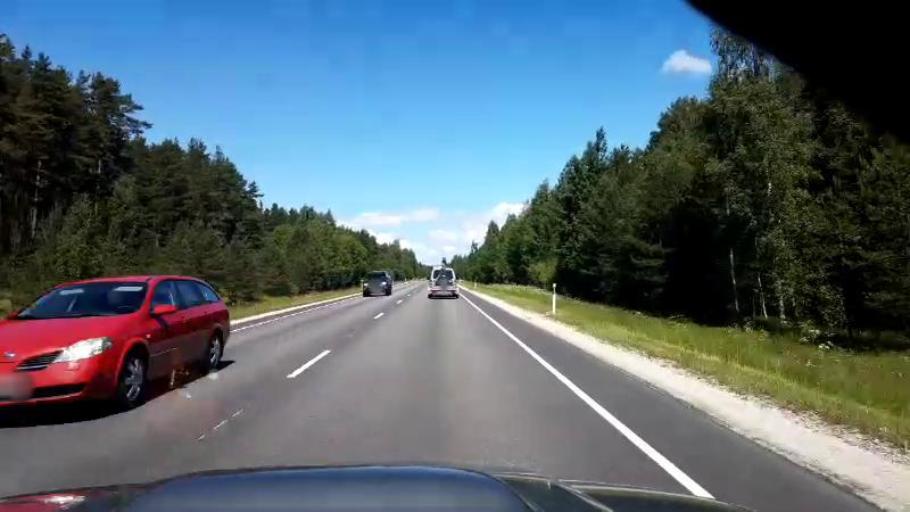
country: LV
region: Salacgrivas
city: Ainazi
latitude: 58.0959
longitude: 24.5080
